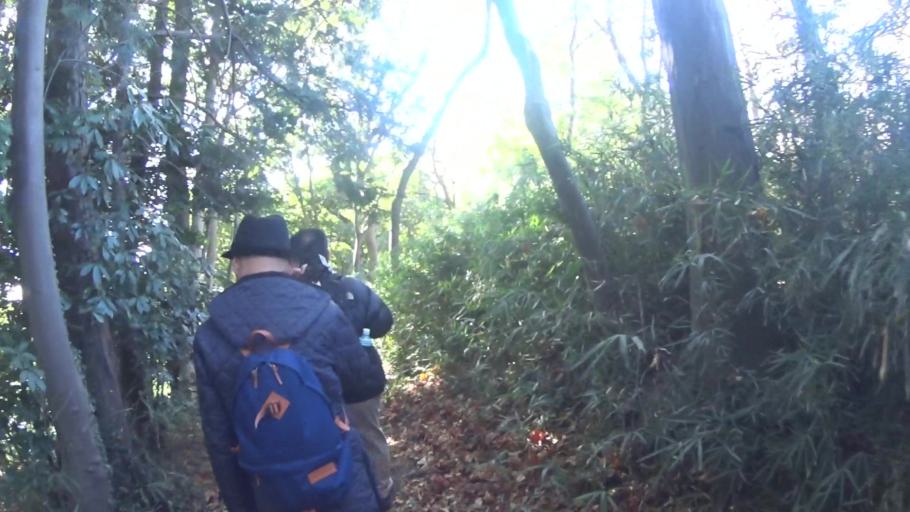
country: JP
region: Tokyo
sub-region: Machida-shi
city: Machida
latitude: 35.6058
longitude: 139.4922
